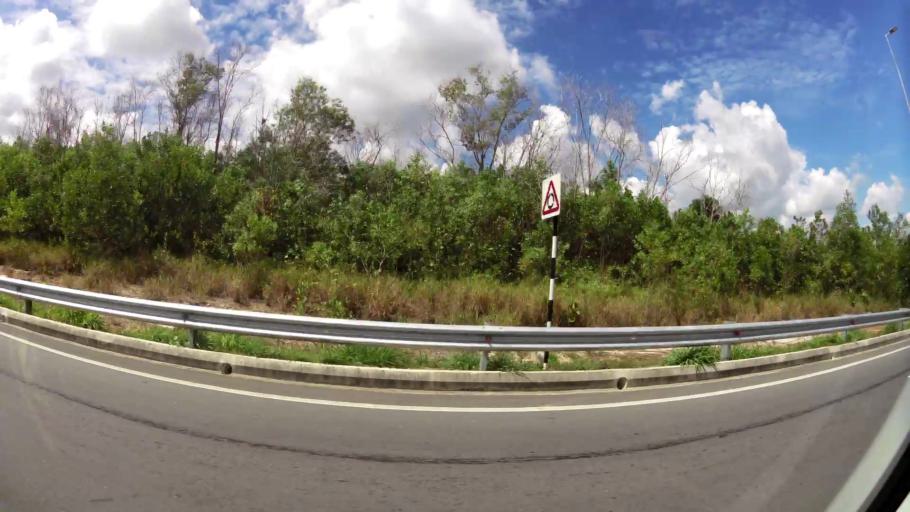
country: BN
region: Brunei and Muara
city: Bandar Seri Begawan
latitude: 4.9326
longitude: 114.8867
